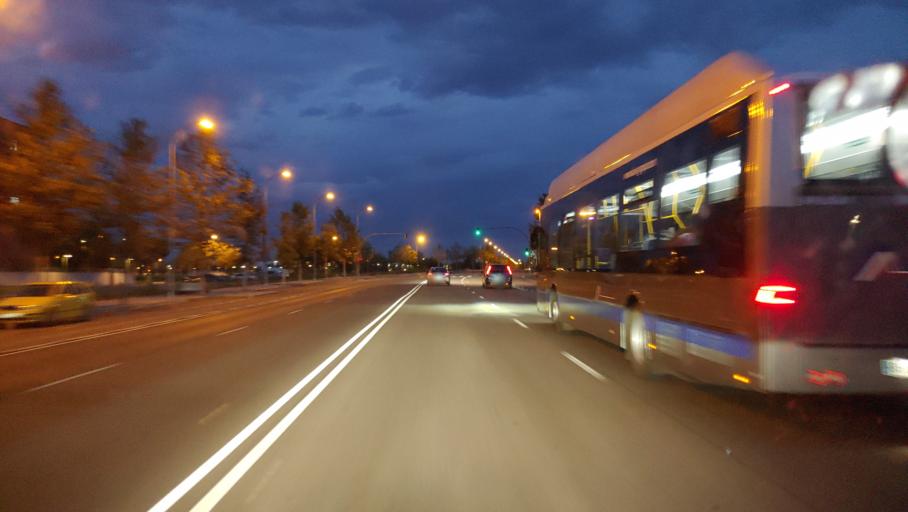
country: ES
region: Castille-La Mancha
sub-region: Provincia de Ciudad Real
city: Ciudad Real
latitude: 38.9693
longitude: -3.9233
